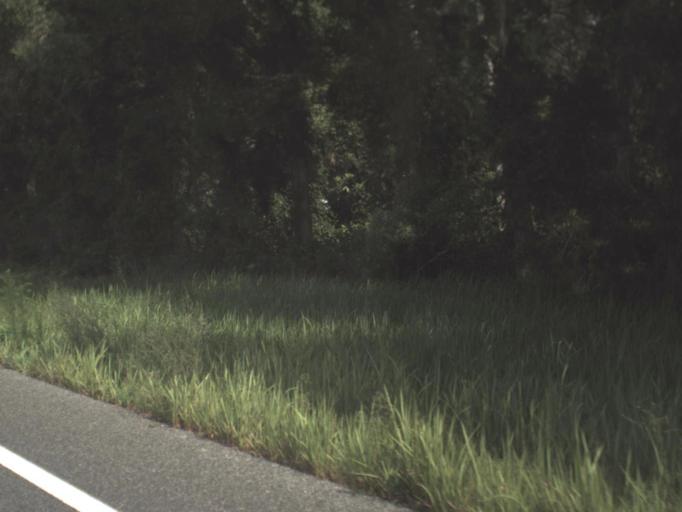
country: US
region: Florida
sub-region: Levy County
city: Chiefland
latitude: 29.4751
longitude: -82.7876
